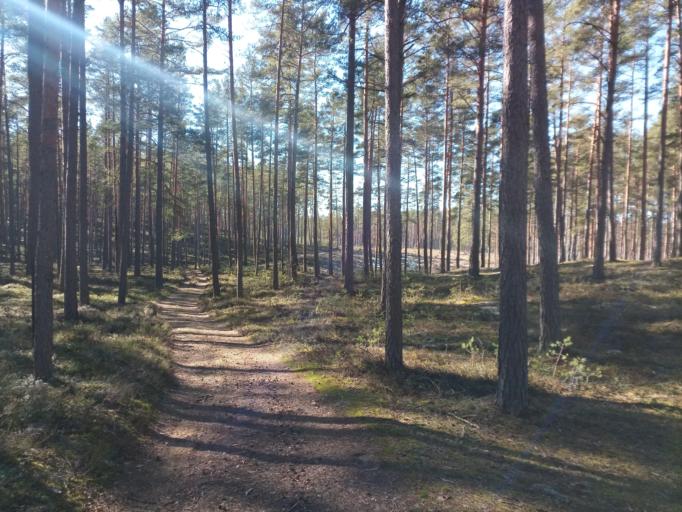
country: LV
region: Carnikava
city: Carnikava
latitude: 57.1683
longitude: 24.3536
